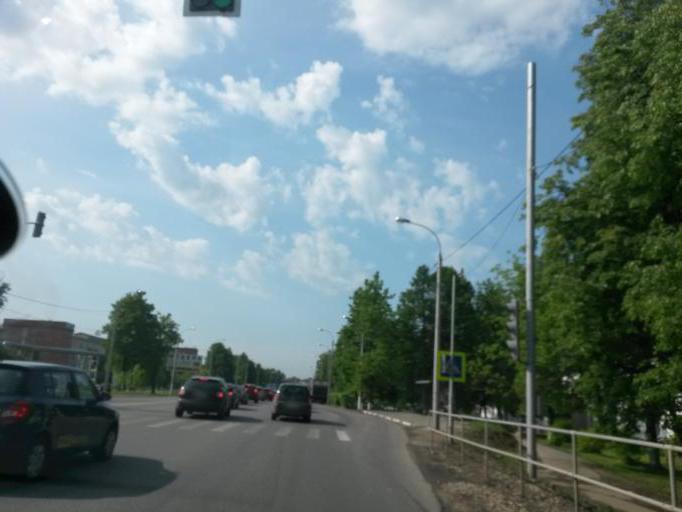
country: RU
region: Moskovskaya
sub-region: Chekhovskiy Rayon
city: Chekhov
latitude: 55.1609
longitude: 37.4654
